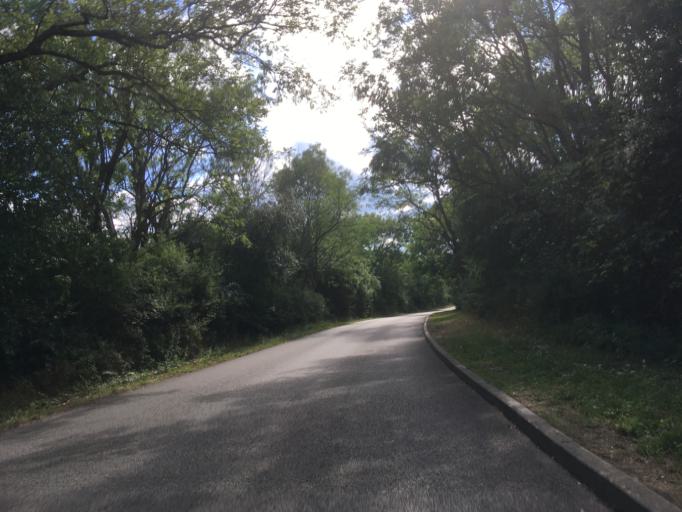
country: DE
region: Brandenburg
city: Oderberg
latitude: 52.9241
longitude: 14.0350
